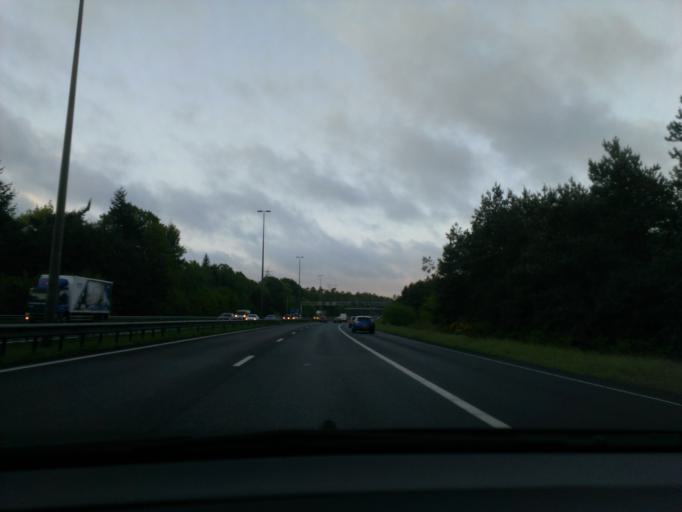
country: NL
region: Gelderland
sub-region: Gemeente Apeldoorn
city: Beekbergen
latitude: 52.1054
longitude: 5.9547
